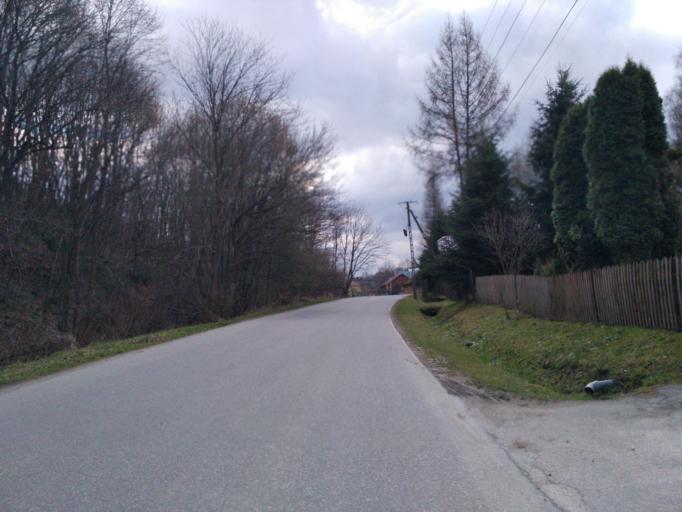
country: PL
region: Subcarpathian Voivodeship
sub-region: Powiat brzozowski
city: Dydnia
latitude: 49.6659
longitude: 22.1926
